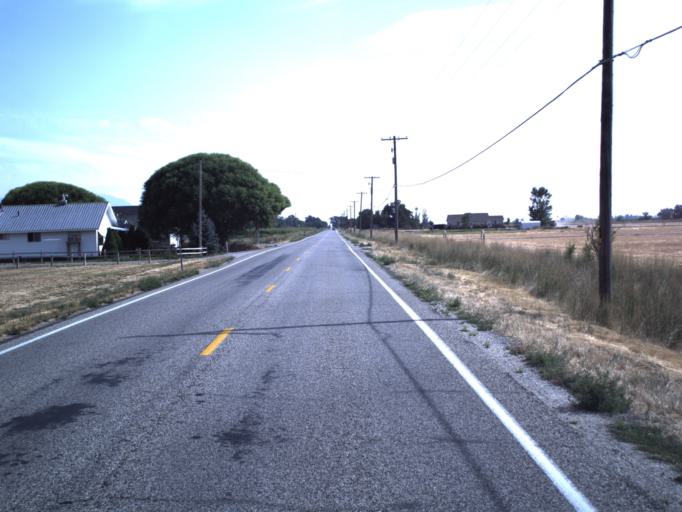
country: US
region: Utah
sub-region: Box Elder County
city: Honeyville
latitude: 41.6831
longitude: -112.0899
